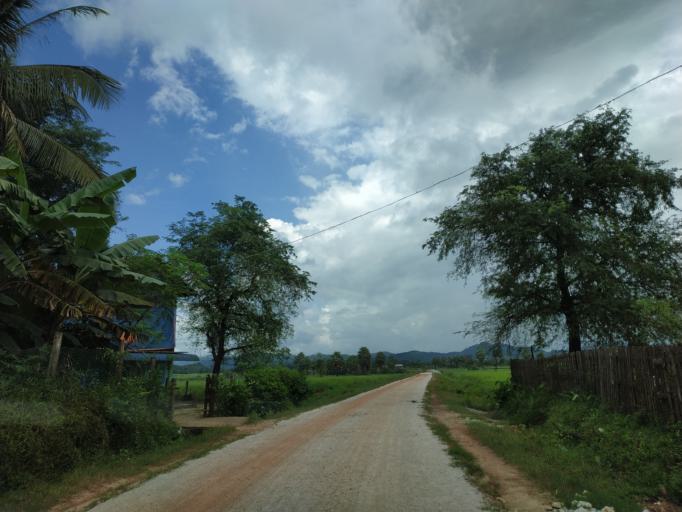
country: MM
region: Tanintharyi
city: Dawei
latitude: 14.1865
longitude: 98.1660
